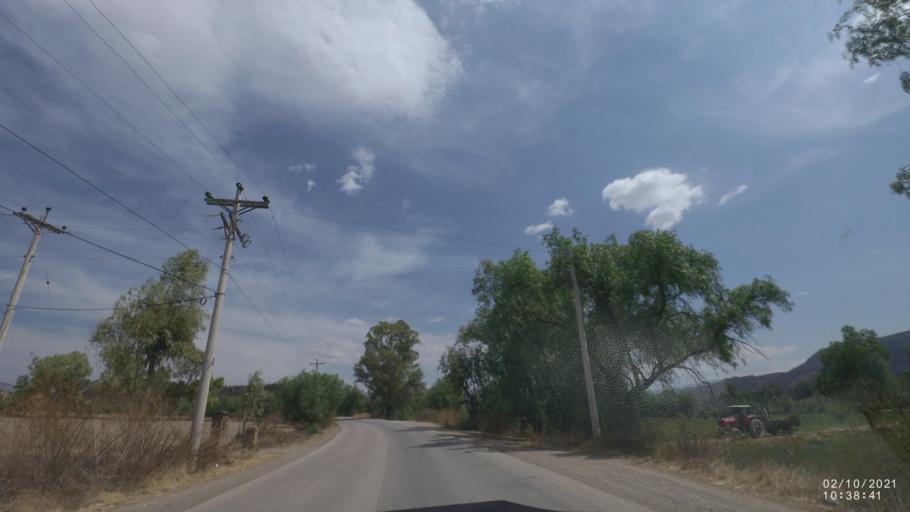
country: BO
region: Cochabamba
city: Capinota
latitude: -17.6321
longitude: -66.2659
